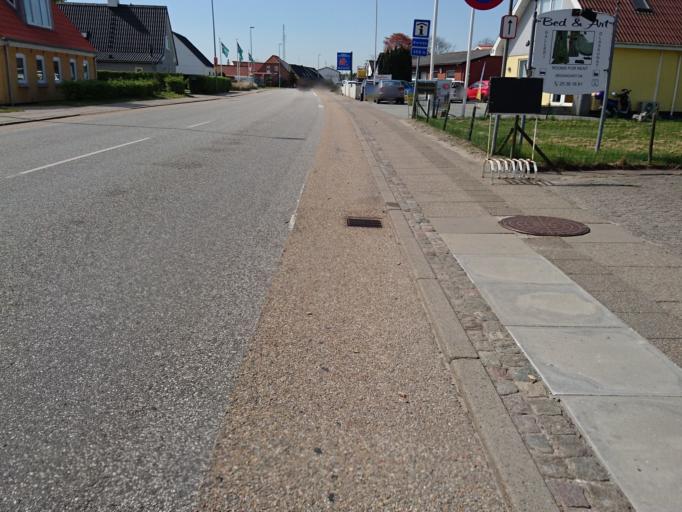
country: DK
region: North Denmark
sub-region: Frederikshavn Kommune
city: Strandby
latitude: 57.5962
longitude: 10.4149
